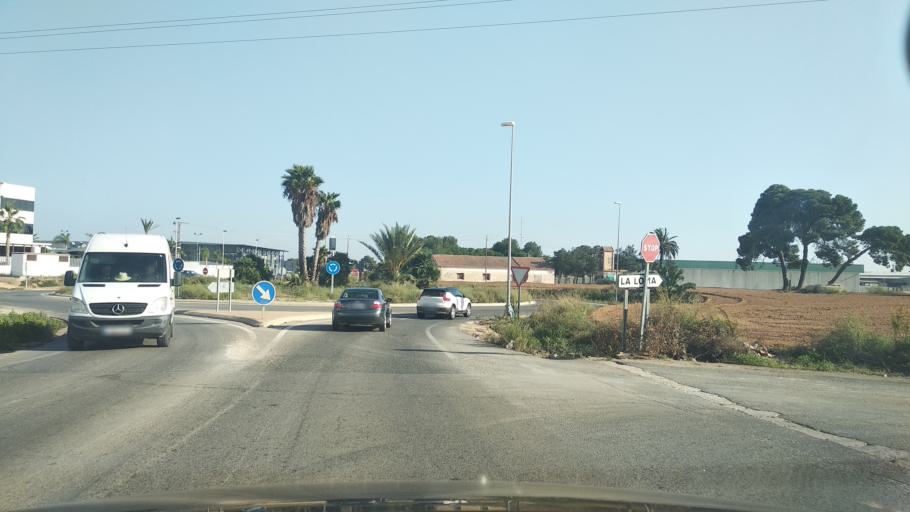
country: ES
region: Murcia
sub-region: Murcia
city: San Javier
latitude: 37.8141
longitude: -0.8412
